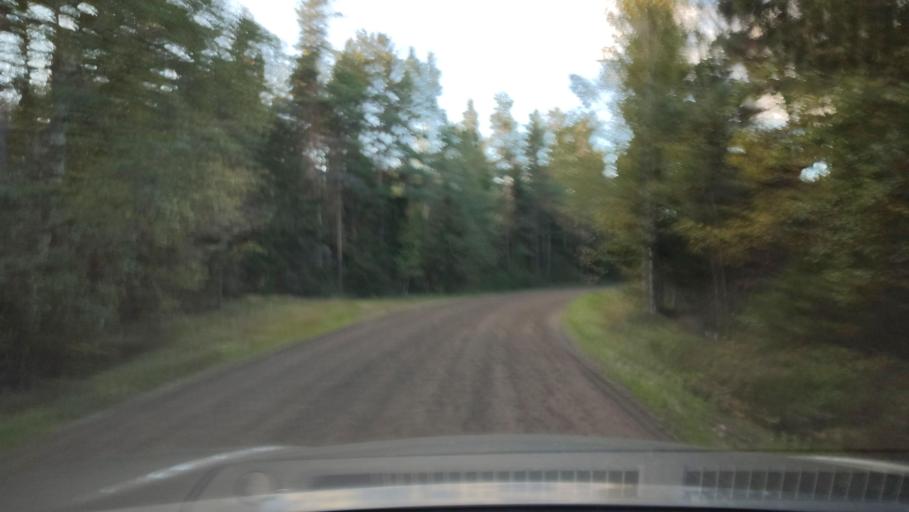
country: FI
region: Southern Ostrobothnia
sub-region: Suupohja
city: Karijoki
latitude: 62.2325
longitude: 21.5715
